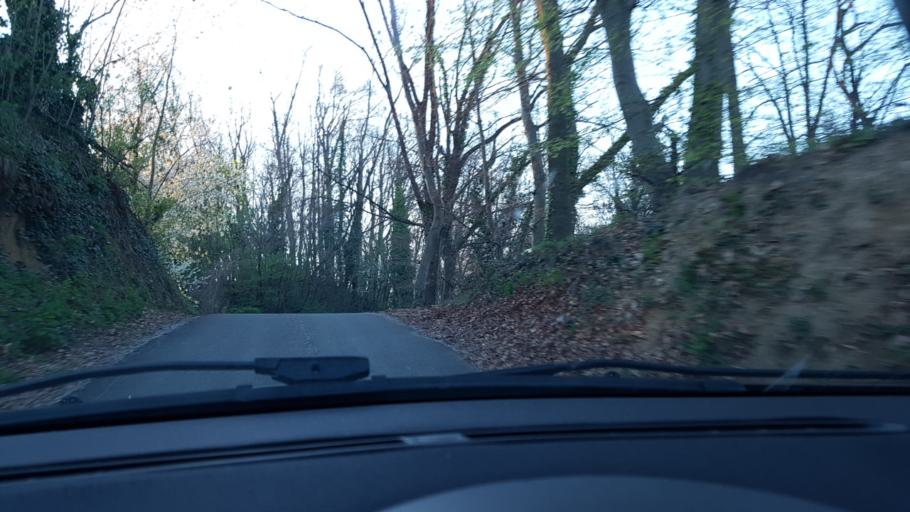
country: HR
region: Krapinsko-Zagorska
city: Pregrada
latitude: 46.1680
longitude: 15.6929
